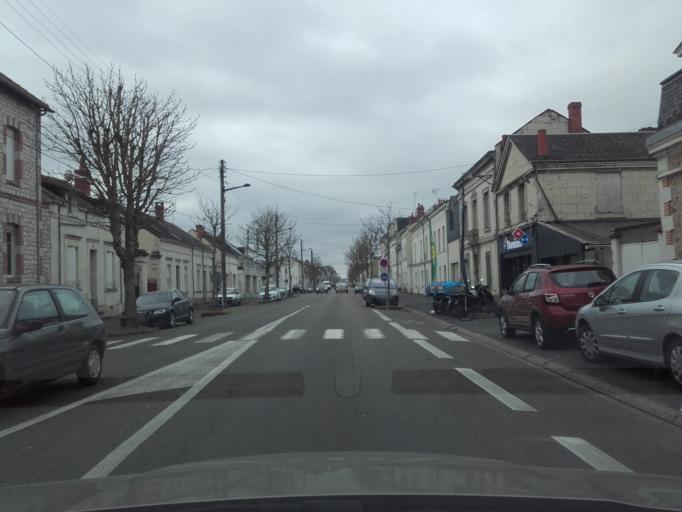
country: FR
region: Pays de la Loire
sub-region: Departement de Maine-et-Loire
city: Saumur
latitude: 47.2733
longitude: -0.0628
